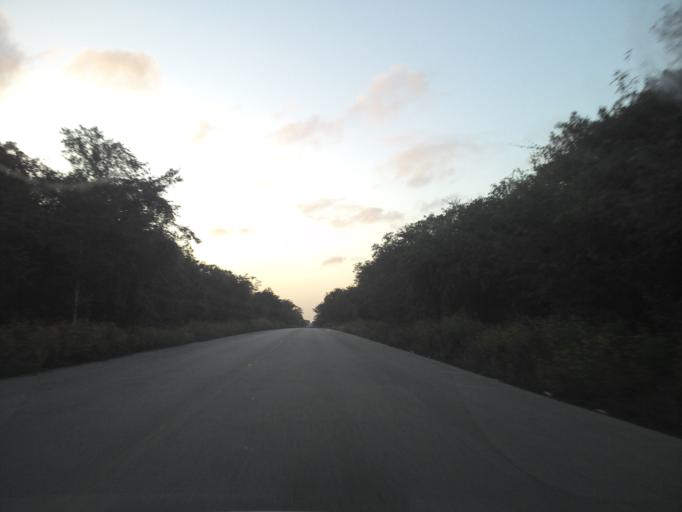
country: MX
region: Quintana Roo
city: Coba
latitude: 20.5132
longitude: -87.7287
